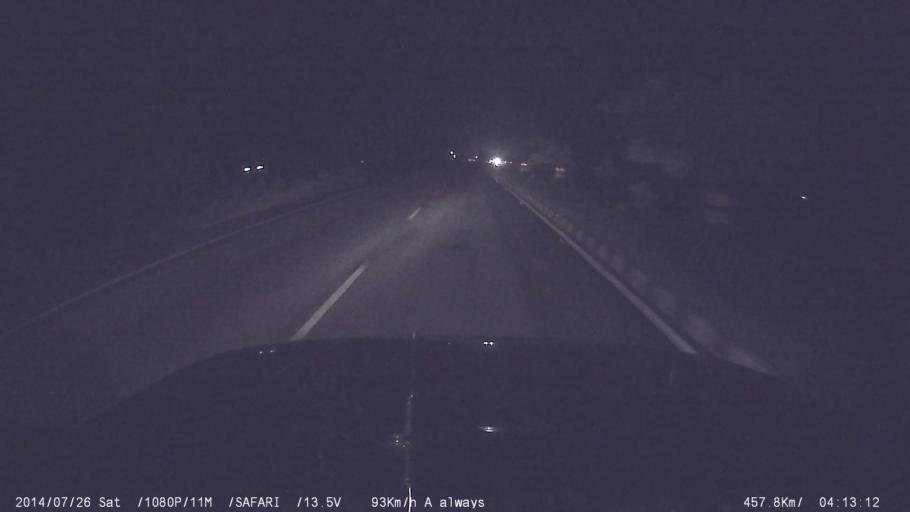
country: IN
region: Kerala
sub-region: Thrissur District
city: Trichur
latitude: 10.4821
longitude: 76.2579
